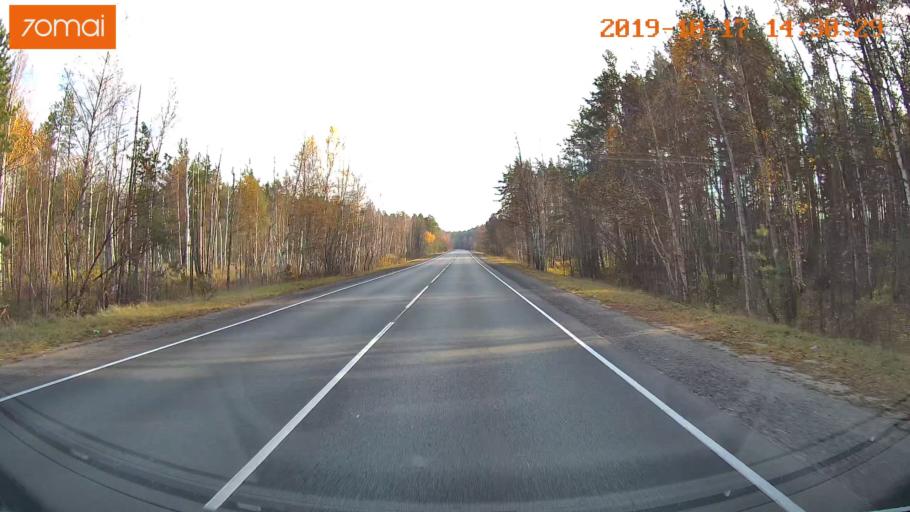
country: RU
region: Rjazan
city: Solotcha
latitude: 54.9471
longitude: 39.9466
